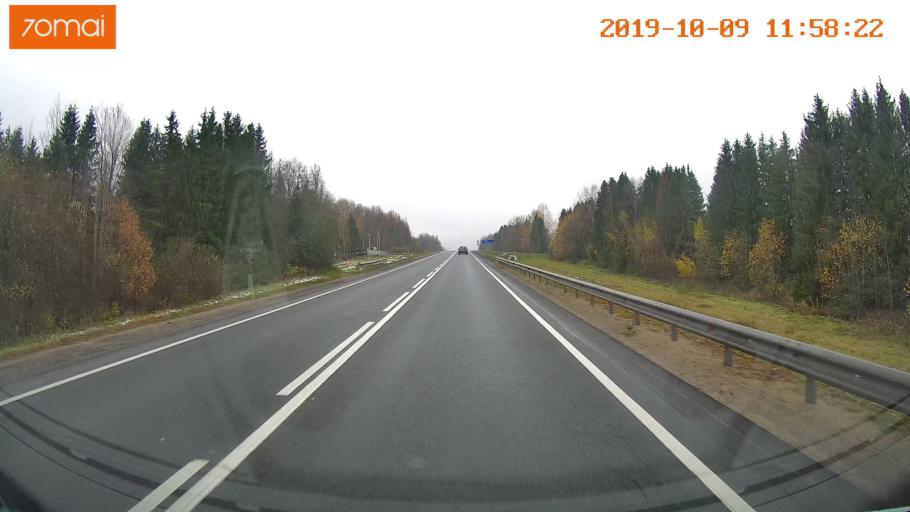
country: RU
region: Vologda
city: Gryazovets
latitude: 58.7190
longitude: 40.2964
